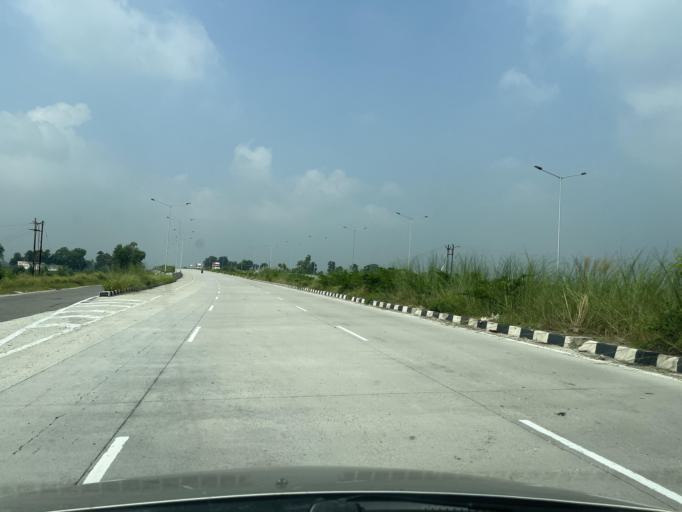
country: IN
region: Uttarakhand
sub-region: Udham Singh Nagar
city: Kashipur
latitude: 29.1666
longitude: 78.9802
